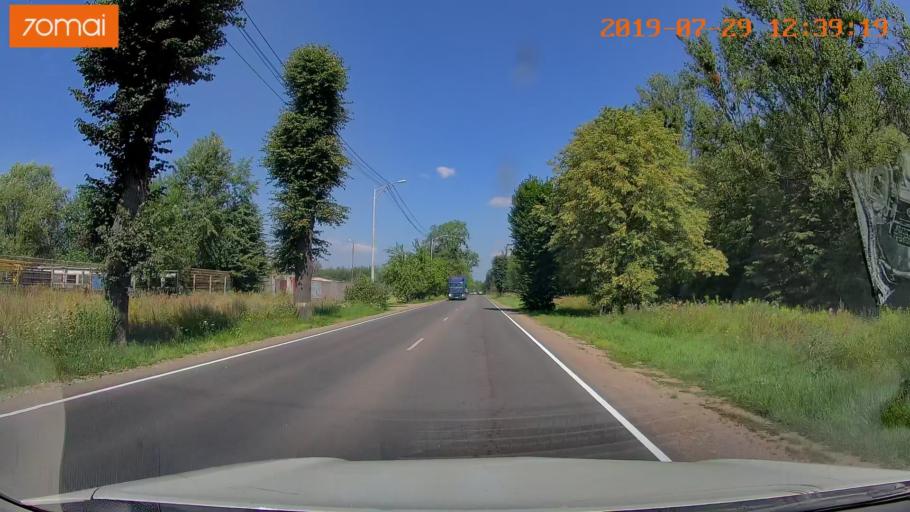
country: RU
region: Kaliningrad
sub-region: Gorod Kaliningrad
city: Kaliningrad
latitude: 54.6587
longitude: 20.5416
